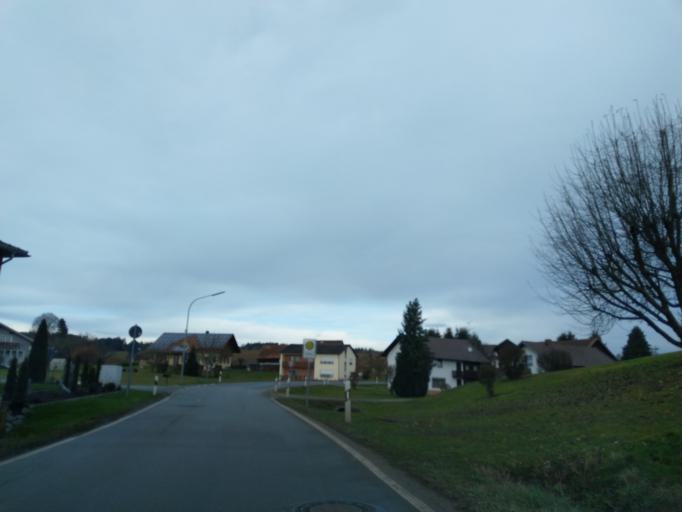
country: DE
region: Bavaria
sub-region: Lower Bavaria
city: Rossbach
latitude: 48.6350
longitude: 12.9655
